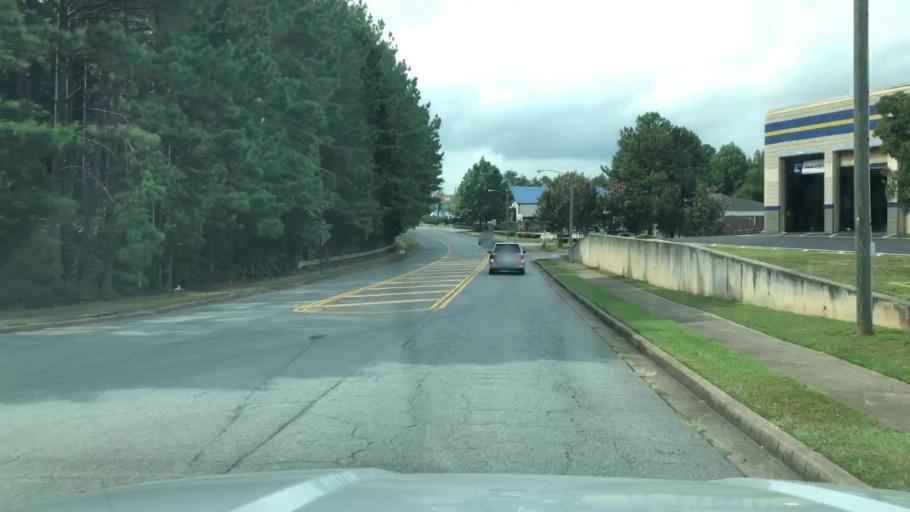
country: US
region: Georgia
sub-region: Fulton County
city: Roswell
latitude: 33.9841
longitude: -84.4246
